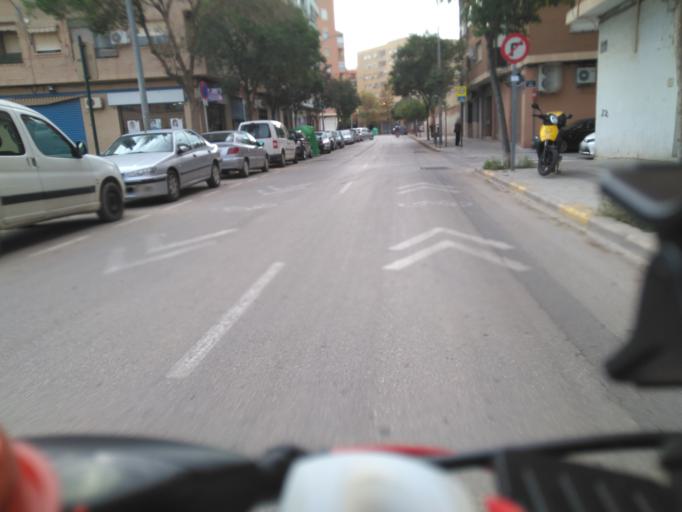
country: ES
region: Valencia
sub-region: Provincia de Valencia
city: Tavernes Blanques
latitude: 39.4920
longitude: -0.3873
